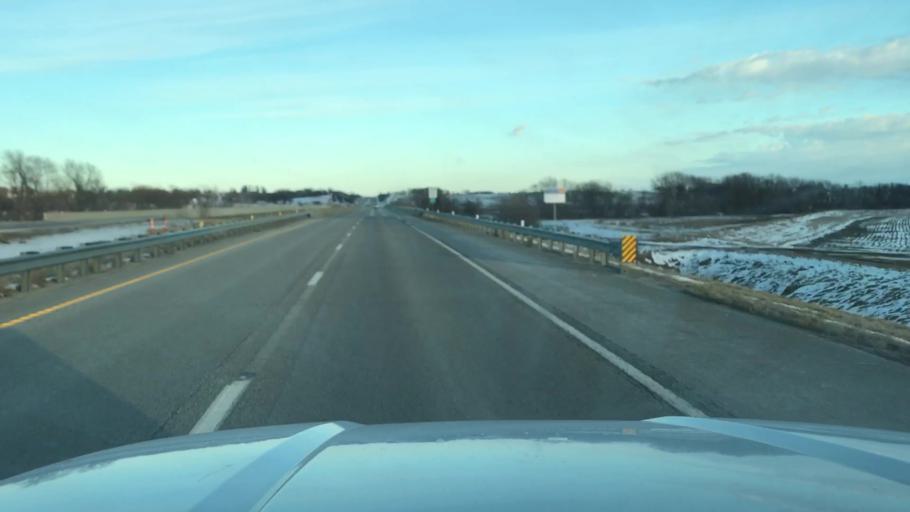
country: US
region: Missouri
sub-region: Buchanan County
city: Saint Joseph
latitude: 39.7478
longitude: -94.7296
